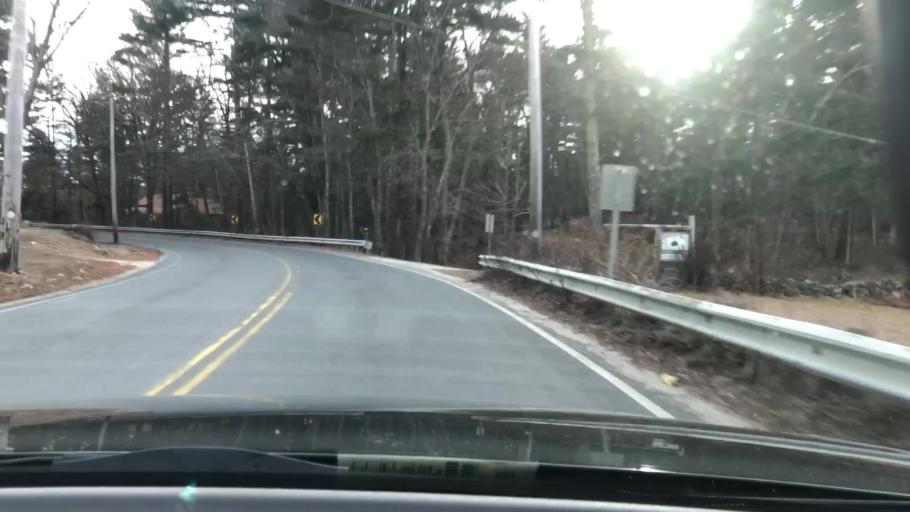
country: US
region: Massachusetts
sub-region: Worcester County
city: Mendon
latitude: 42.0684
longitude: -71.5252
